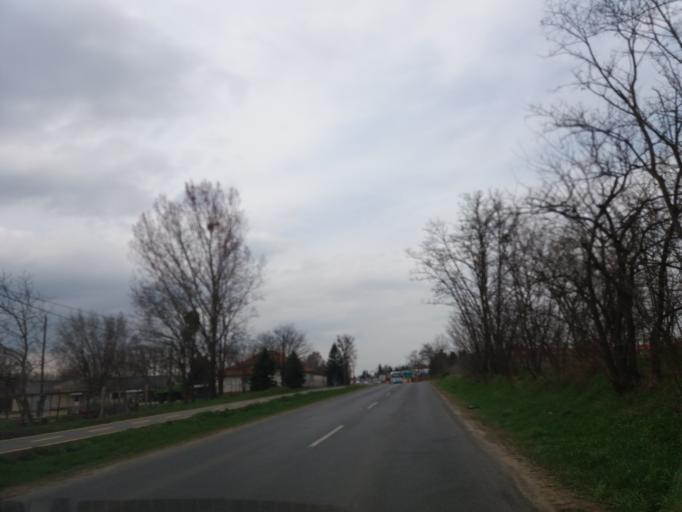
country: HU
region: Szabolcs-Szatmar-Bereg
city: Kisvarda
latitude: 48.1972
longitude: 22.0956
